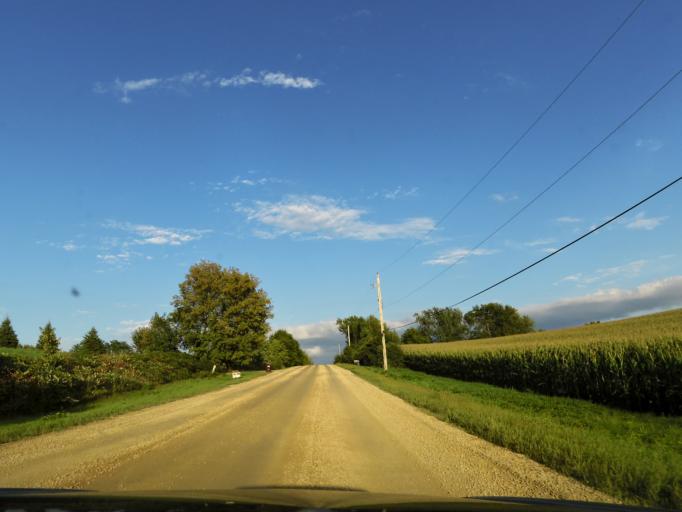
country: US
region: Minnesota
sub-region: Washington County
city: Cottage Grove
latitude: 44.8765
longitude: -92.8749
